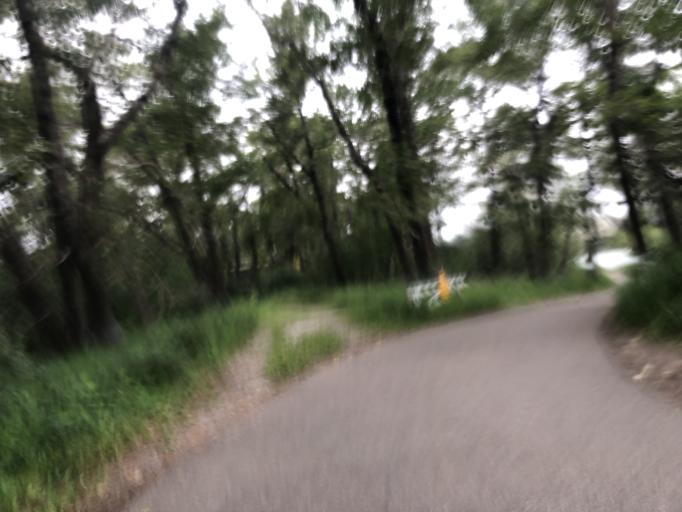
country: CA
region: Alberta
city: Calgary
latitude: 51.0434
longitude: -114.0172
